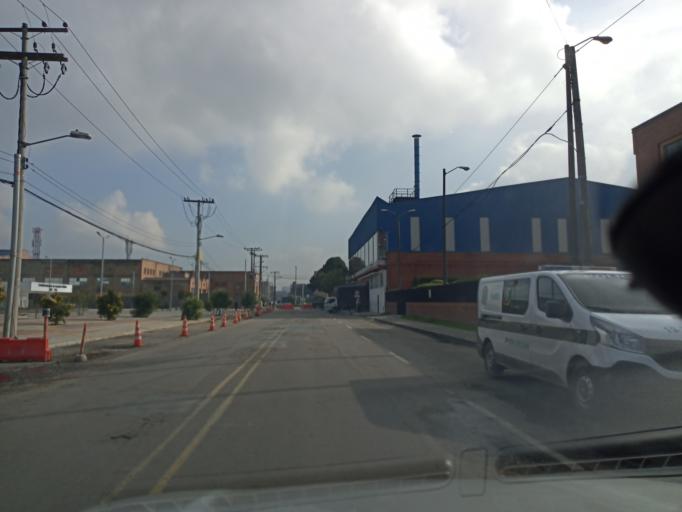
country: CO
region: Bogota D.C.
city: Bogota
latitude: 4.6299
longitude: -74.1123
